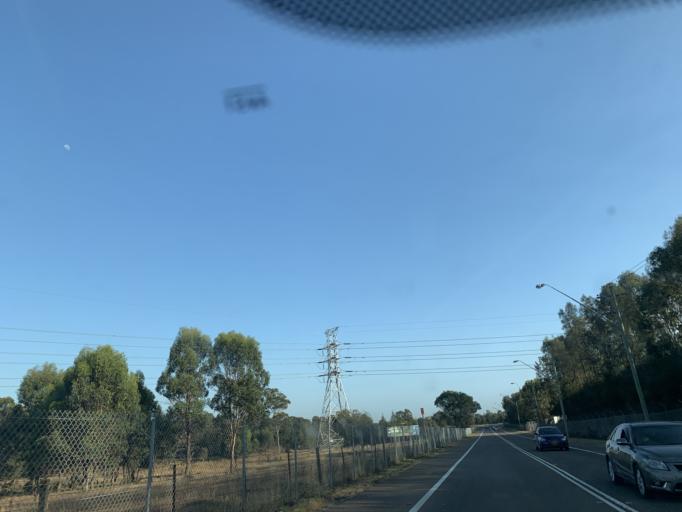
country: AU
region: New South Wales
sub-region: Fairfield
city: Horsley Park
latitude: -33.8066
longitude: 150.8641
